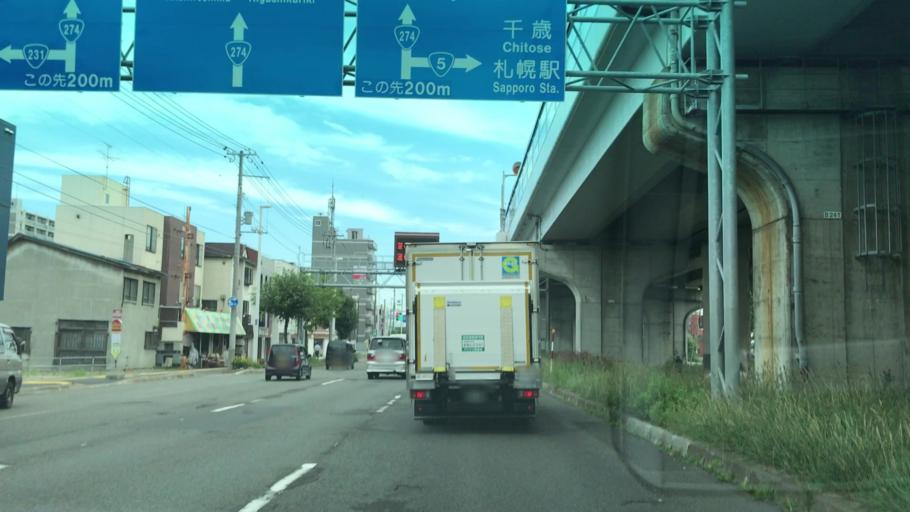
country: JP
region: Hokkaido
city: Sapporo
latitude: 43.1011
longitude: 141.3422
